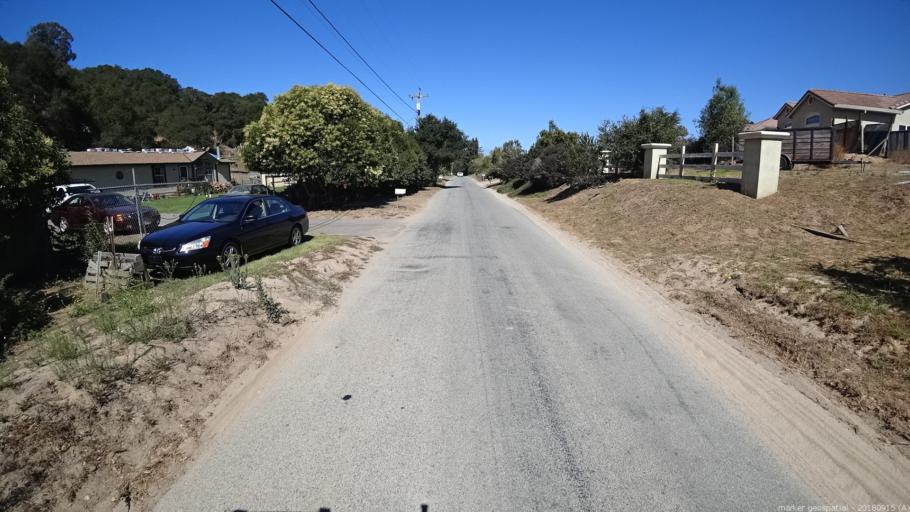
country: US
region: California
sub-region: Monterey County
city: Las Lomas
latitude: 36.8469
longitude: -121.7072
